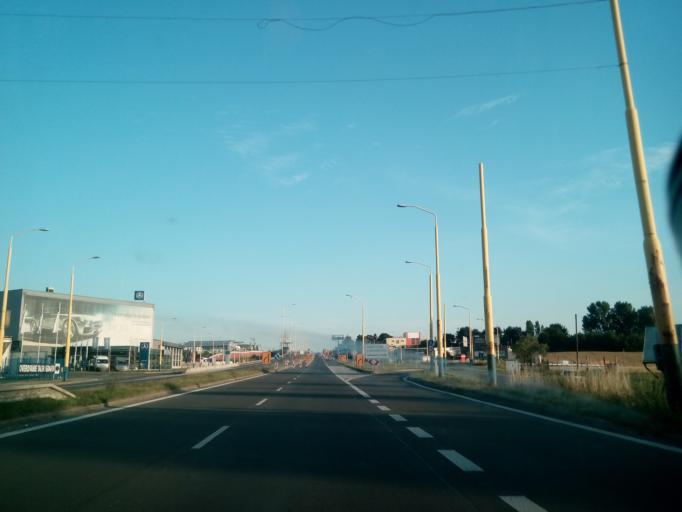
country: SK
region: Presovsky
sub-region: Okres Presov
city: Presov
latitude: 48.9611
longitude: 21.2560
